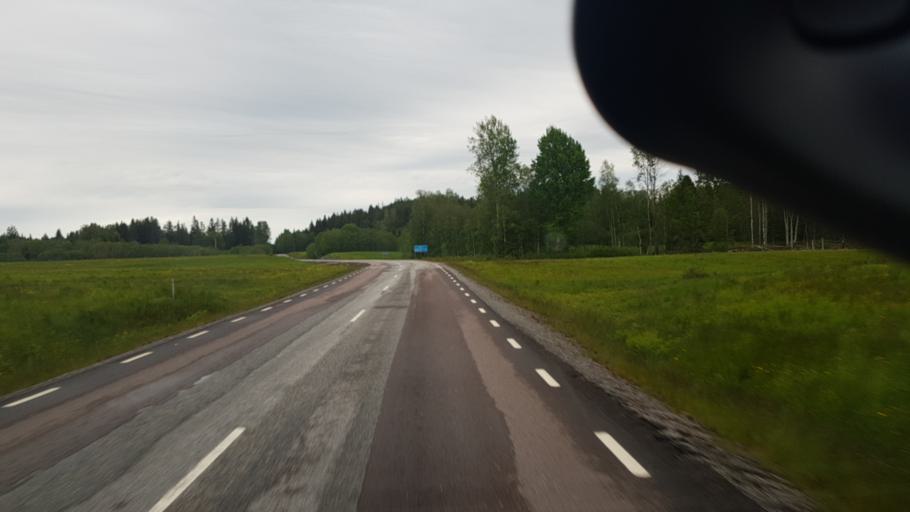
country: SE
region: Vaermland
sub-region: Arjangs Kommun
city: Arjaeng
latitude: 59.5592
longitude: 12.1202
